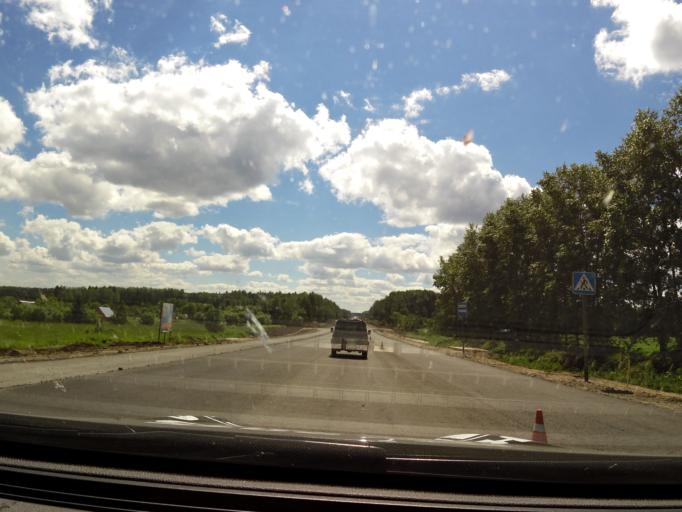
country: RU
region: Vologda
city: Molochnoye
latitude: 59.3673
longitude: 39.6720
